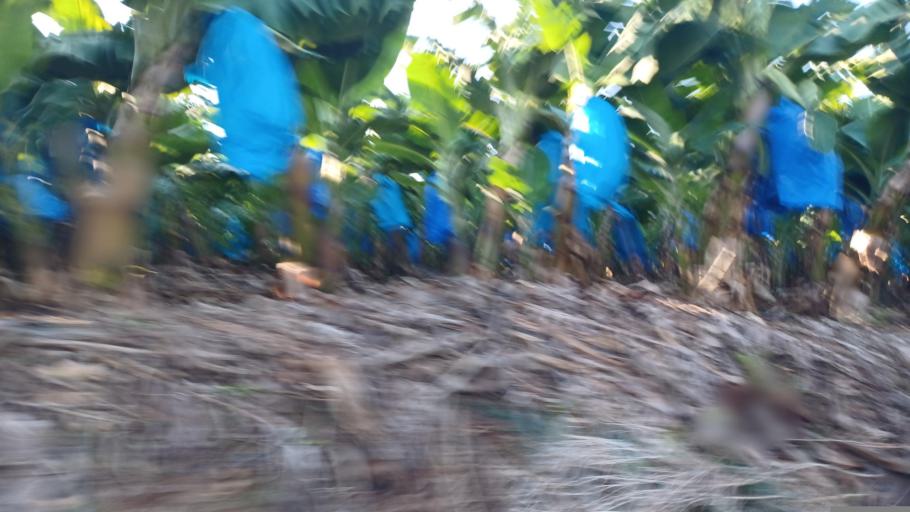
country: CY
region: Pafos
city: Kissonerga
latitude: 34.8332
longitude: 32.3947
